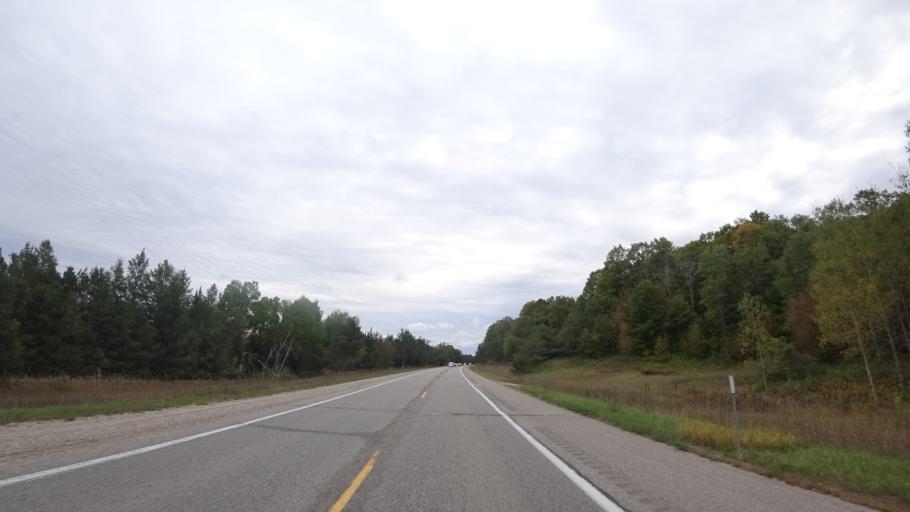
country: US
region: Michigan
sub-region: Charlevoix County
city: Boyne City
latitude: 45.2363
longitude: -84.9163
